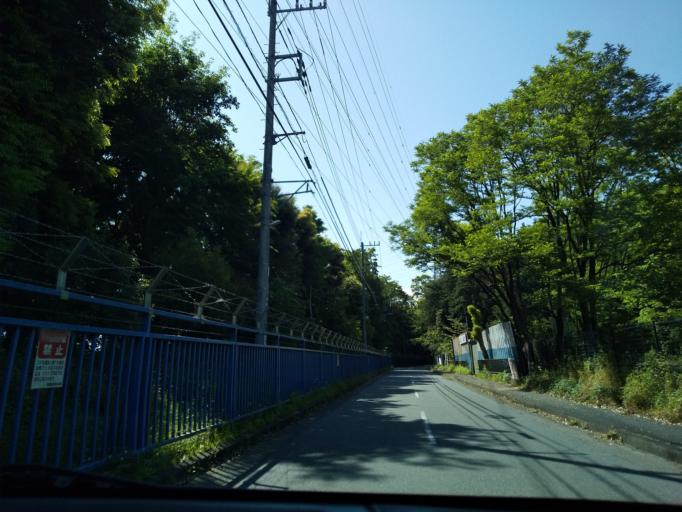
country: JP
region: Kanagawa
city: Zama
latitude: 35.5449
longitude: 139.3880
